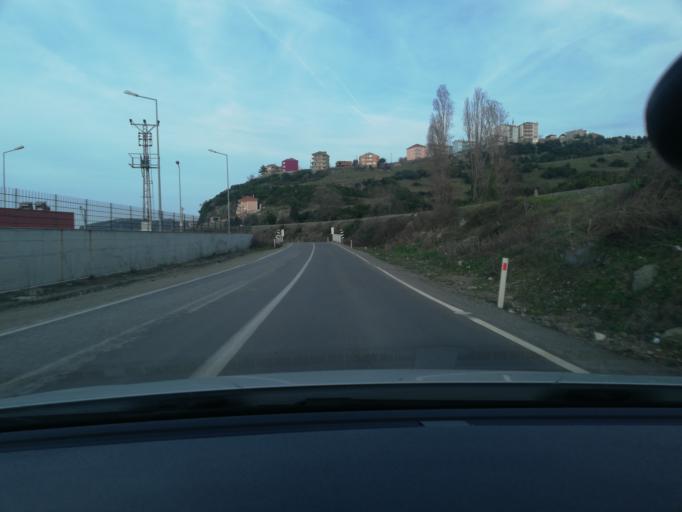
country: TR
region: Zonguldak
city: Tieum
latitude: 41.5544
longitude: 32.0100
